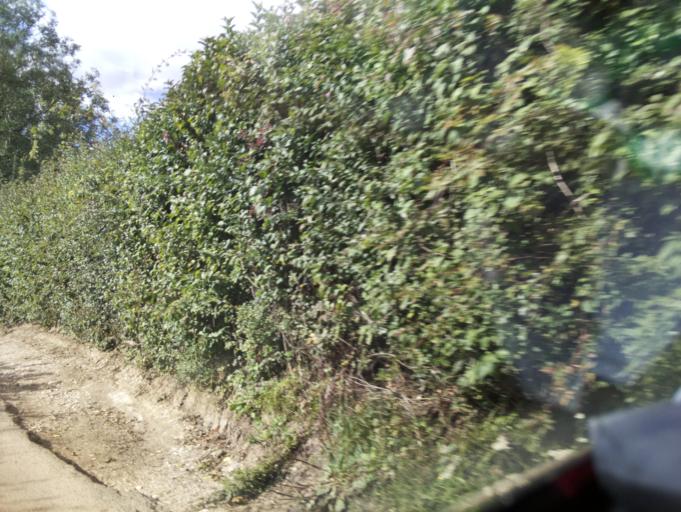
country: GB
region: England
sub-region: Hampshire
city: Chandlers Ford
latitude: 51.0543
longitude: -1.3808
